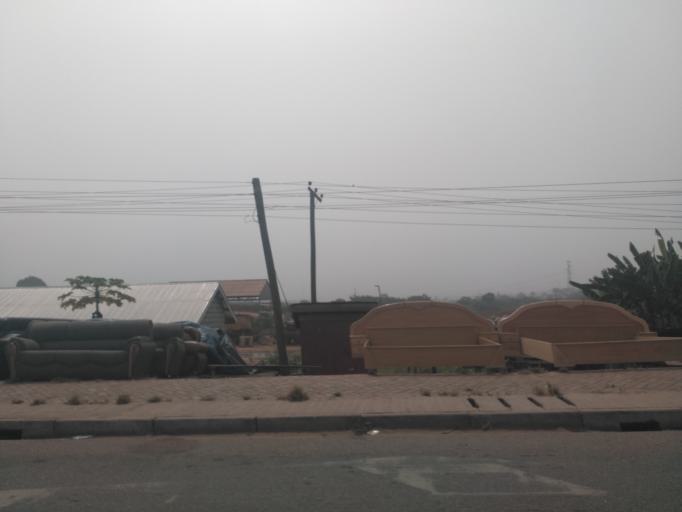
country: GH
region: Ashanti
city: Kumasi
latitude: 6.6683
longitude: -1.6100
